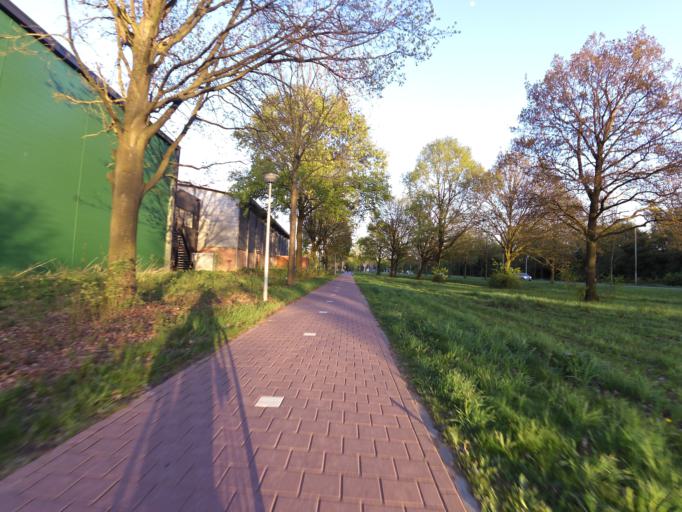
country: NL
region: Gelderland
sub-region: Gemeente Doetinchem
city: Doetinchem
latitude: 51.9633
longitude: 6.2703
